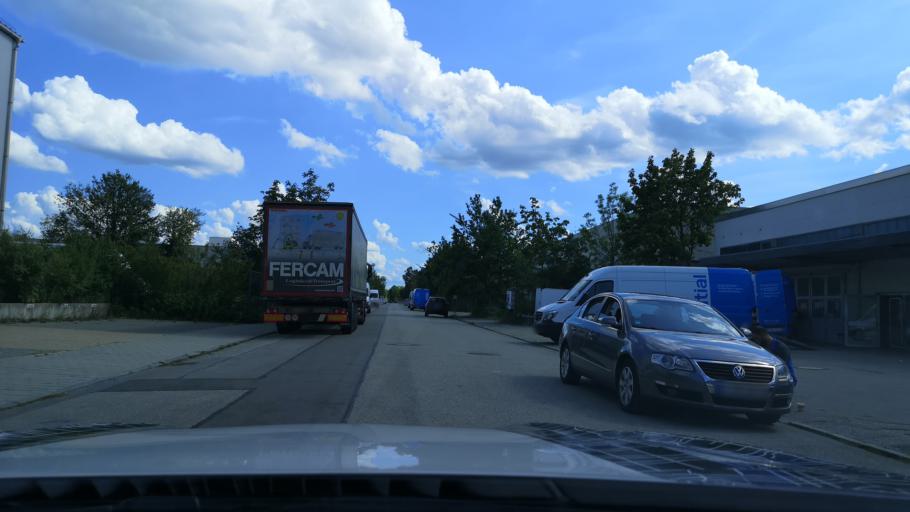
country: DE
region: Bavaria
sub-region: Upper Bavaria
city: Kirchheim bei Muenchen
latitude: 48.1790
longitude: 11.7667
